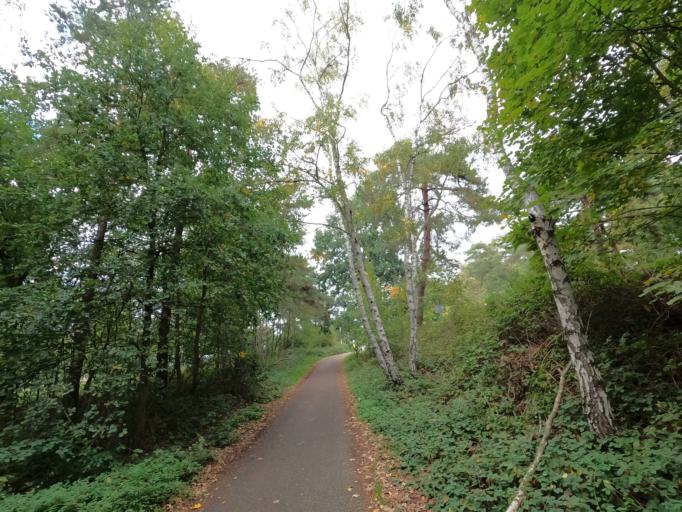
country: BE
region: Flanders
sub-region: Provincie Antwerpen
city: Dessel
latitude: 51.2244
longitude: 5.0935
